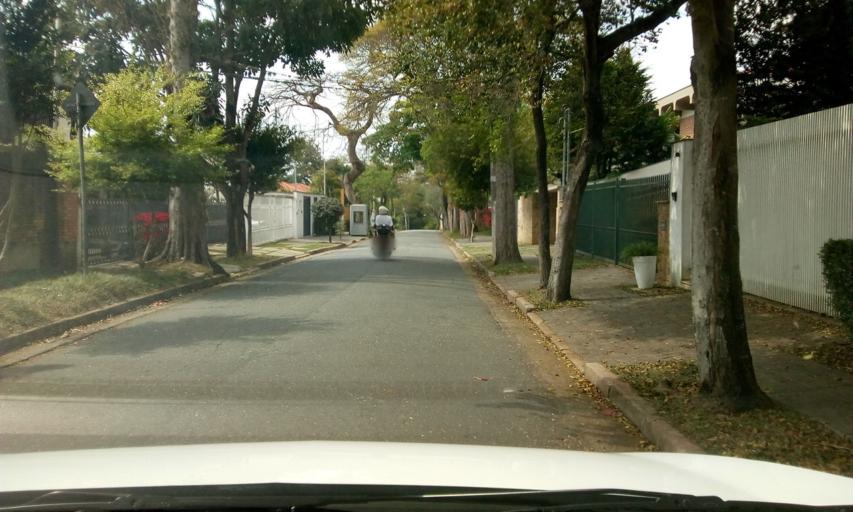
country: BR
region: Sao Paulo
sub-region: Taboao Da Serra
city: Taboao da Serra
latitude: -23.5903
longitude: -46.7265
